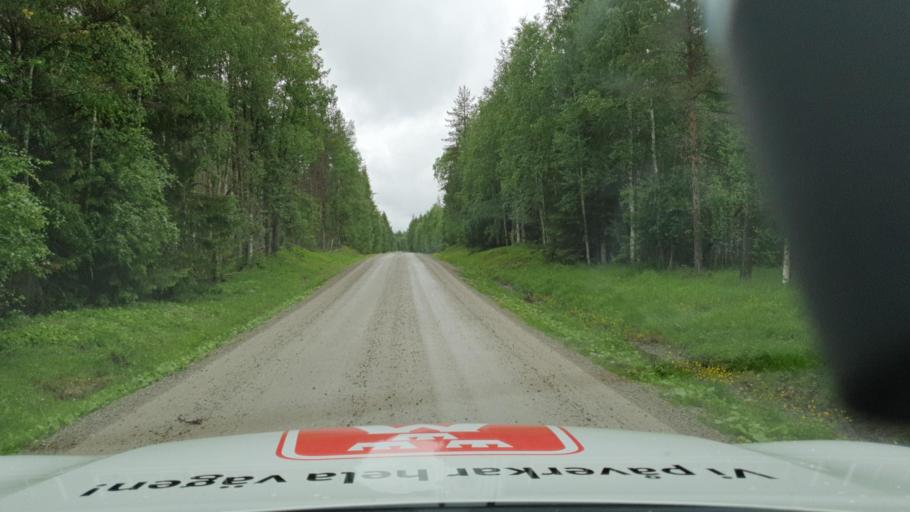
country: SE
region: Vaesterbotten
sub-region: Dorotea Kommun
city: Dorotea
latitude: 63.9942
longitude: 16.8016
